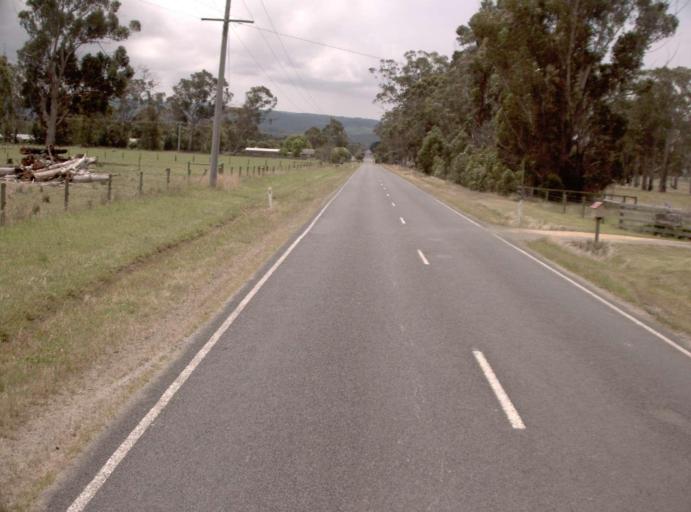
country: AU
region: Victoria
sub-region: Latrobe
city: Traralgon
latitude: -38.5318
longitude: 146.6585
